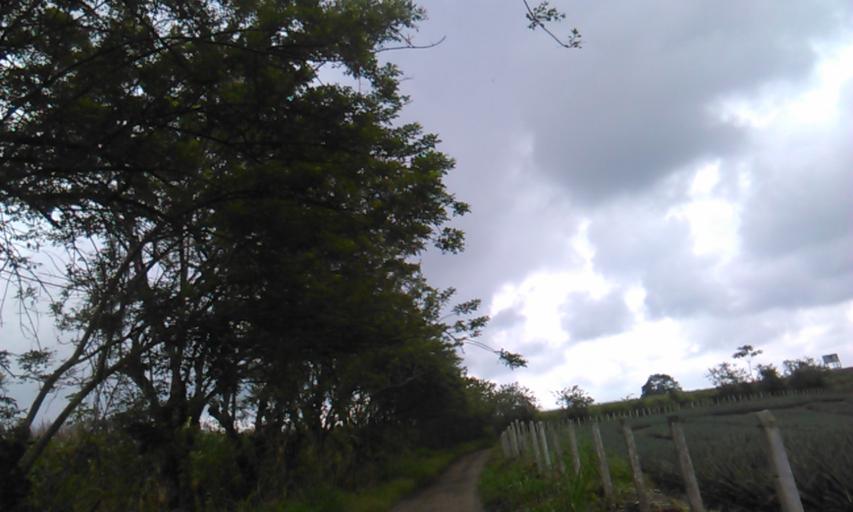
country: CO
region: Quindio
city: La Tebaida
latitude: 4.5032
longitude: -75.8566
